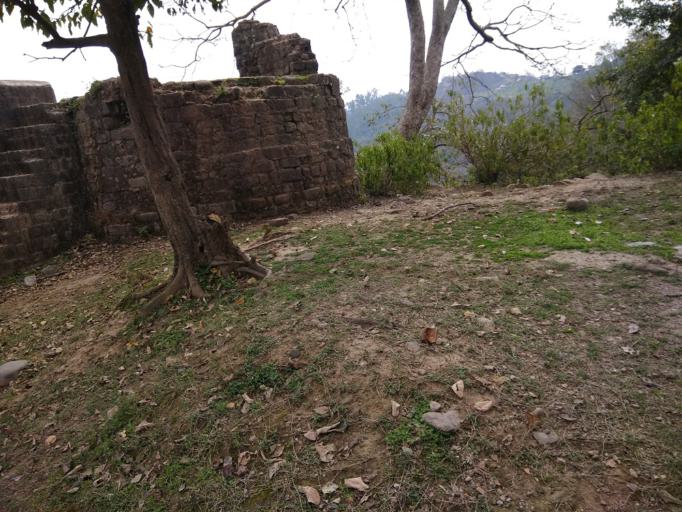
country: IN
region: Himachal Pradesh
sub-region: Kangra
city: Kotla
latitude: 32.2354
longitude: 76.0454
